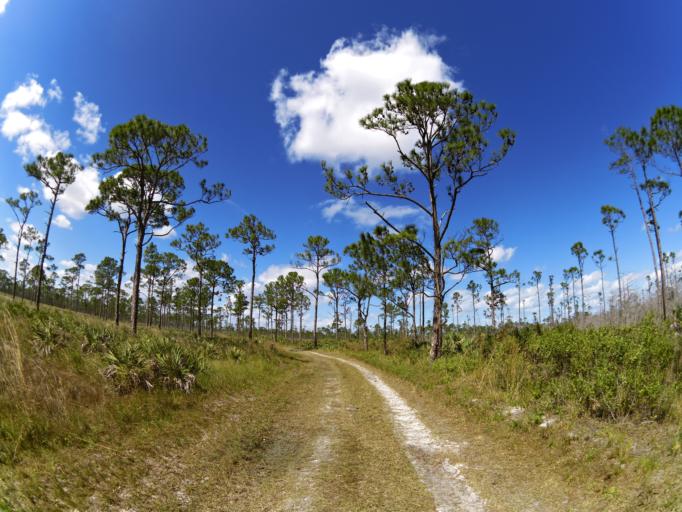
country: US
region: Florida
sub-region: Martin County
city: Hobe Sound
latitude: 27.0166
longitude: -80.1430
